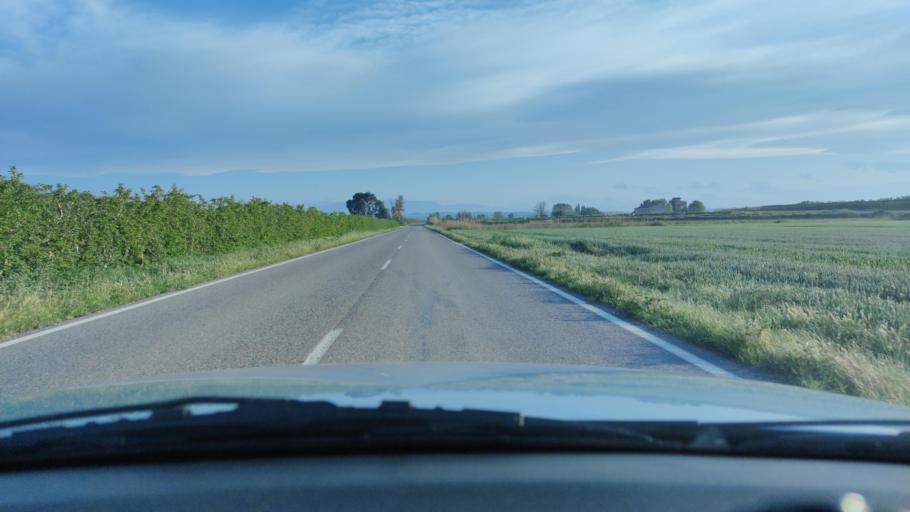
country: ES
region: Catalonia
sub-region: Provincia de Lleida
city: Penelles
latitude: 41.7223
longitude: 0.9827
